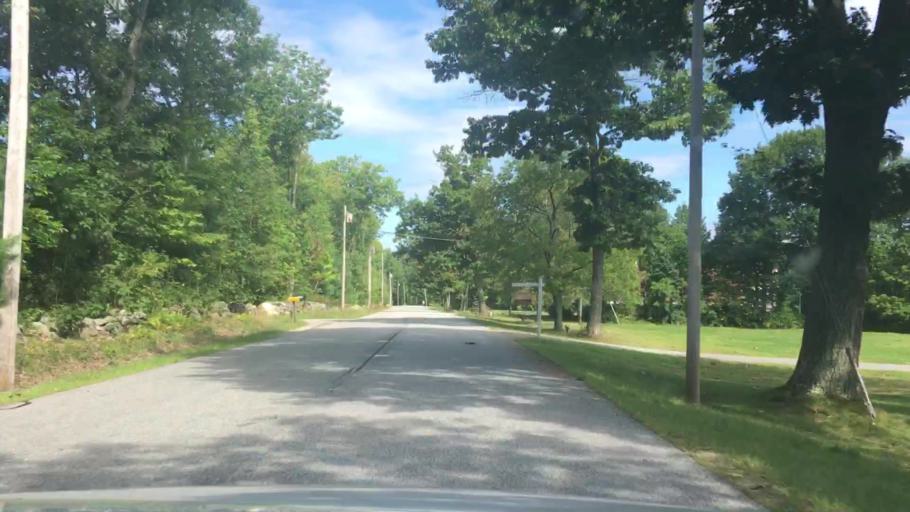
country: US
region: Maine
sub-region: Androscoggin County
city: Turner
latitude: 44.1762
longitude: -70.2526
